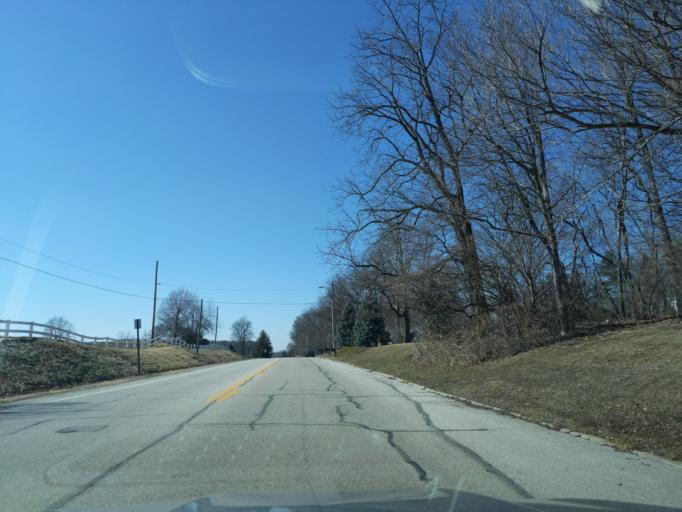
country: US
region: Indiana
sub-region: Tippecanoe County
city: West Lafayette
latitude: 40.4389
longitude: -86.9196
